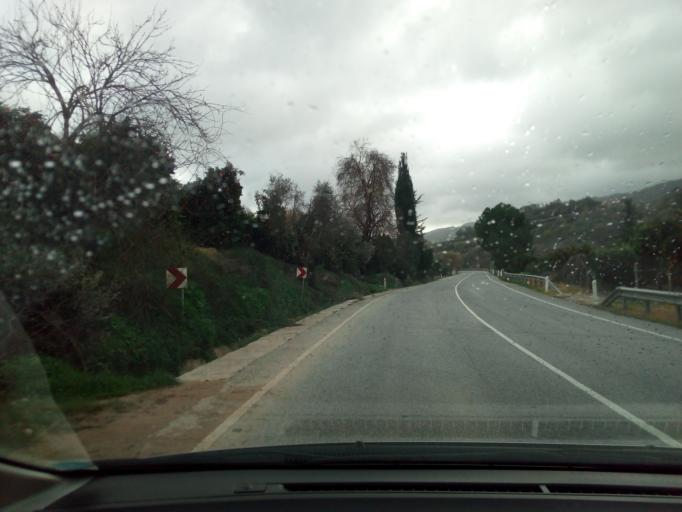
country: CY
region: Pafos
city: Polis
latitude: 34.9426
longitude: 32.4702
